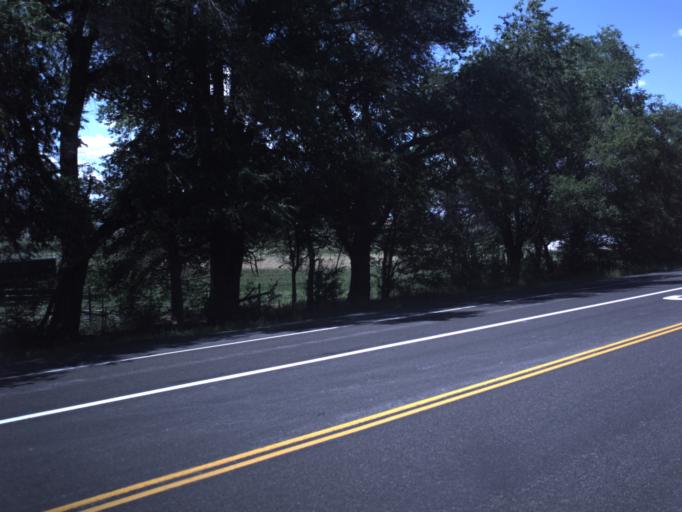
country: US
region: Utah
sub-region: Emery County
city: Castle Dale
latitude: 39.2557
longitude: -110.9845
